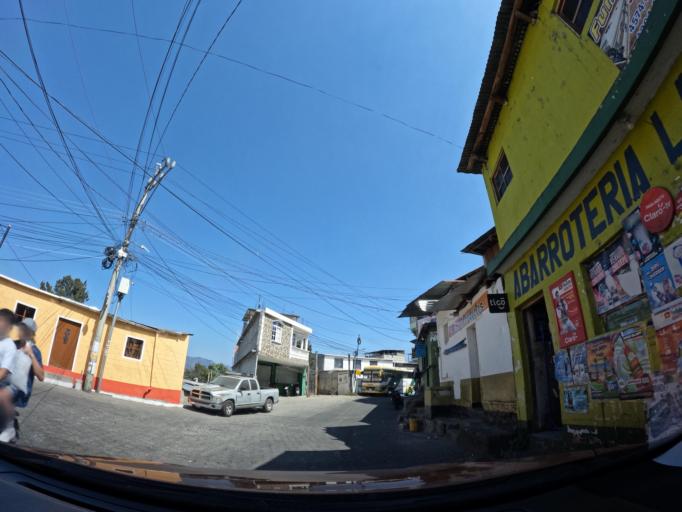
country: GT
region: Solola
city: San Pedro La Laguna
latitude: 14.6900
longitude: -91.2681
